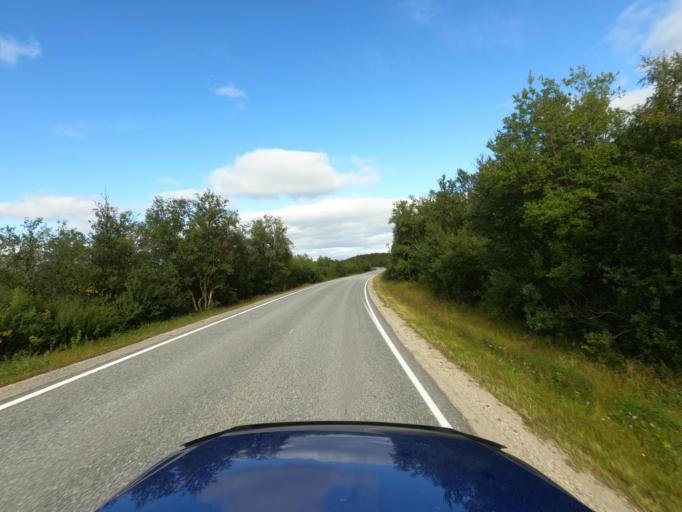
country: NO
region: Finnmark Fylke
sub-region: Porsanger
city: Lakselv
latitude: 70.0173
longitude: 24.9645
